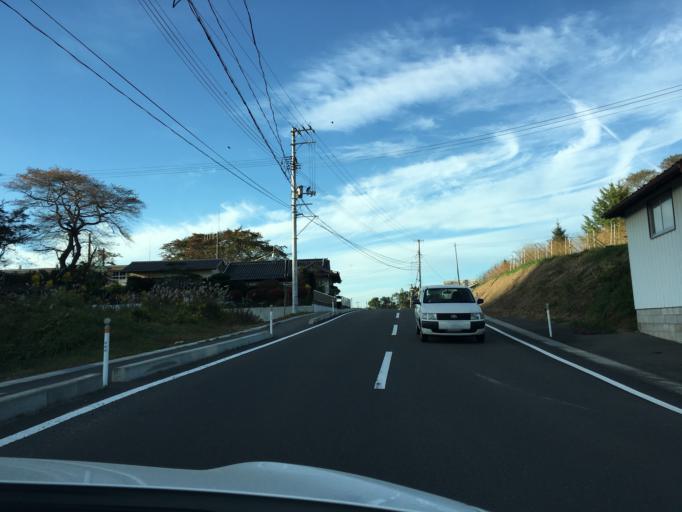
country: JP
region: Fukushima
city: Ishikawa
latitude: 37.2354
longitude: 140.5656
